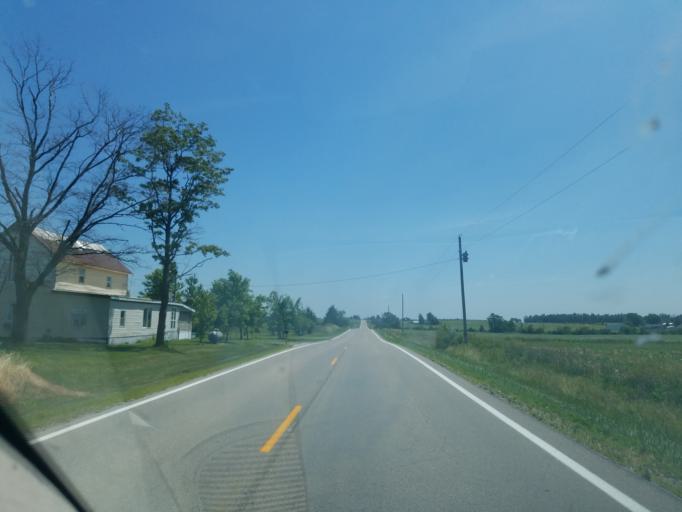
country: US
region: Ohio
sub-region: Mercer County
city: Rockford
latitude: 40.7422
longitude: -84.6840
